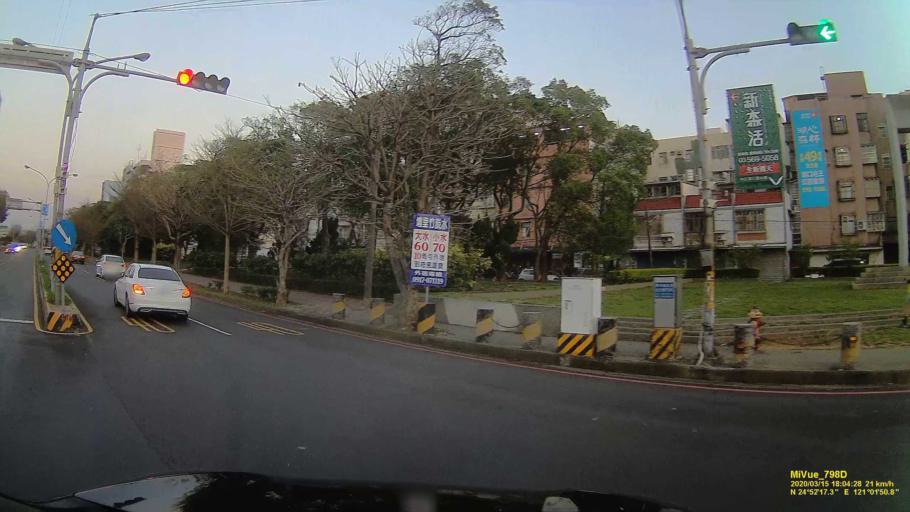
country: TW
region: Taiwan
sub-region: Hsinchu
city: Zhubei
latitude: 24.8715
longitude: 121.0310
